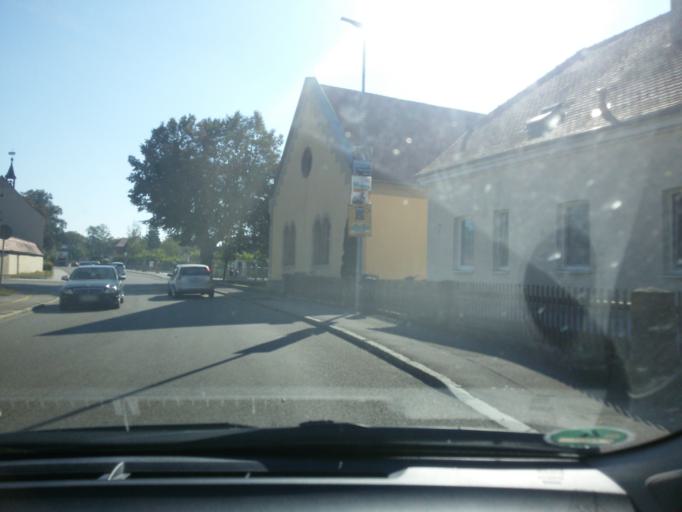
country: DE
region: Bavaria
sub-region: Regierungsbezirk Mittelfranken
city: Wassertrudingen
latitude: 49.0451
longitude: 10.5956
